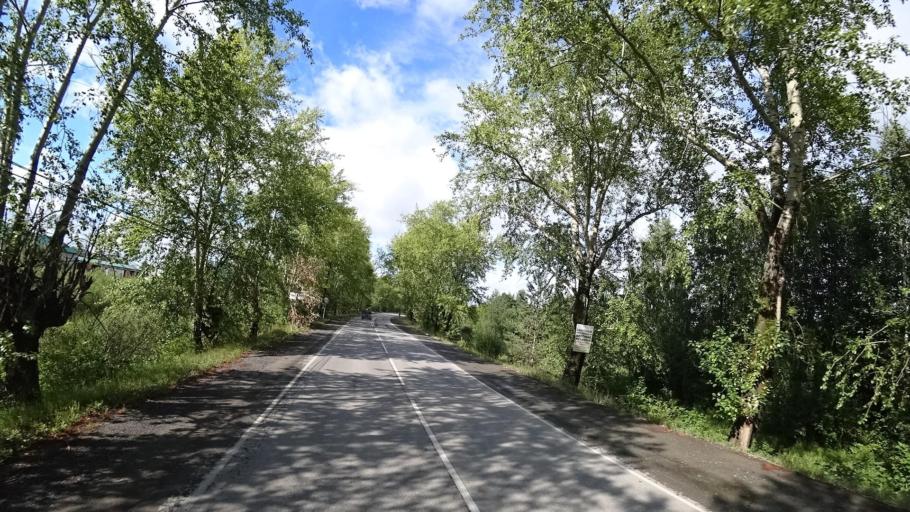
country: RU
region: Sverdlovsk
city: Kamyshlov
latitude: 56.8336
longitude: 62.6963
